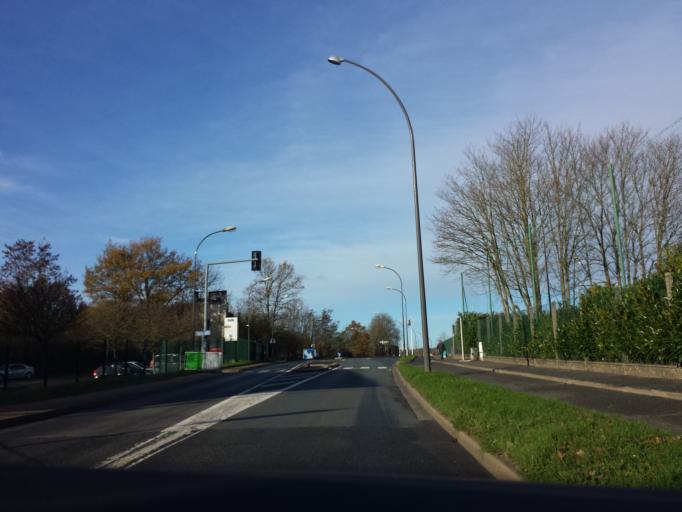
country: FR
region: Ile-de-France
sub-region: Departement de l'Essonne
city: Palaiseau
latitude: 48.7305
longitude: 2.2462
